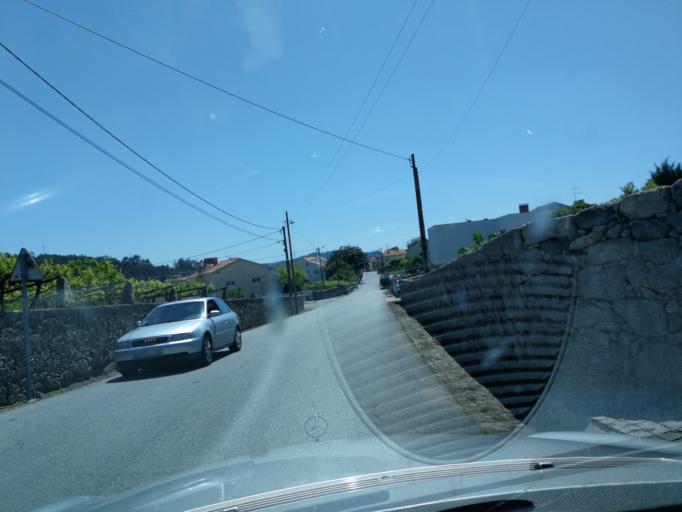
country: PT
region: Viana do Castelo
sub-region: Viana do Castelo
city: Meadela
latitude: 41.7345
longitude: -8.7860
